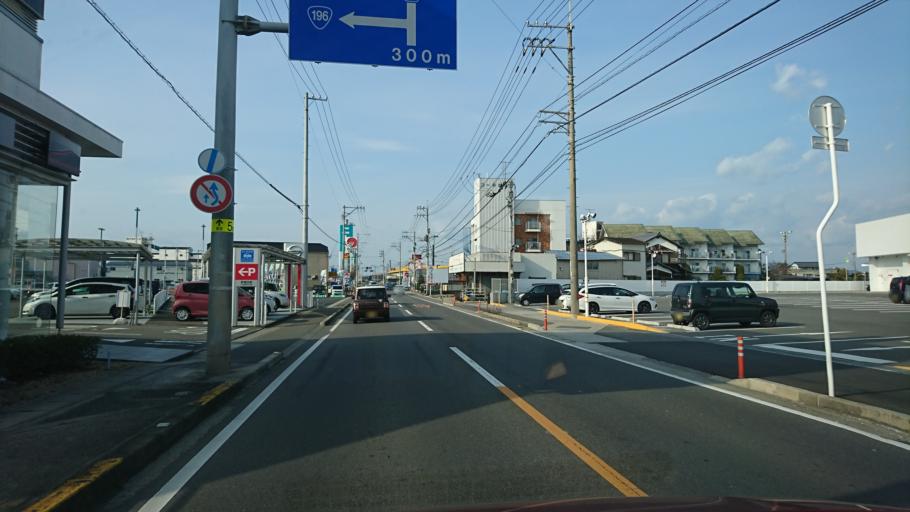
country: JP
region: Ehime
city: Saijo
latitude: 34.0355
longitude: 133.0338
